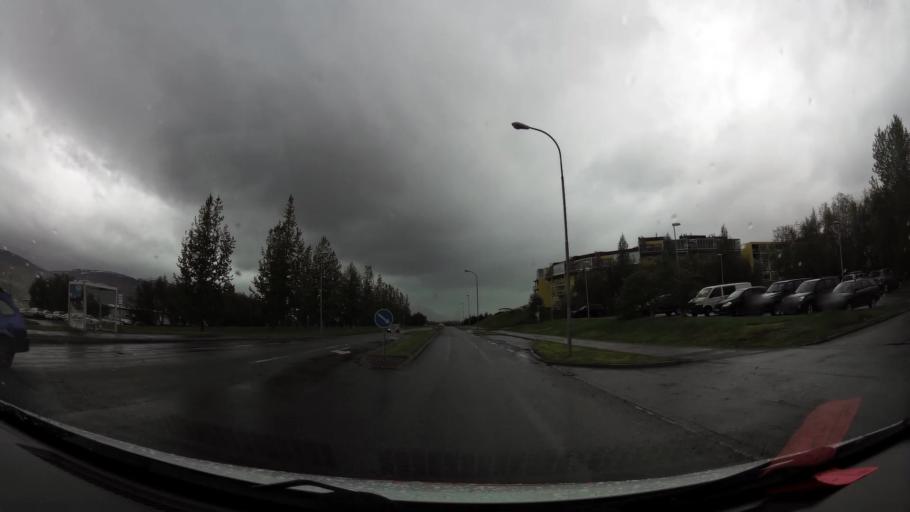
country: IS
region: Northeast
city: Akureyri
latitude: 65.6738
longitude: -18.0971
